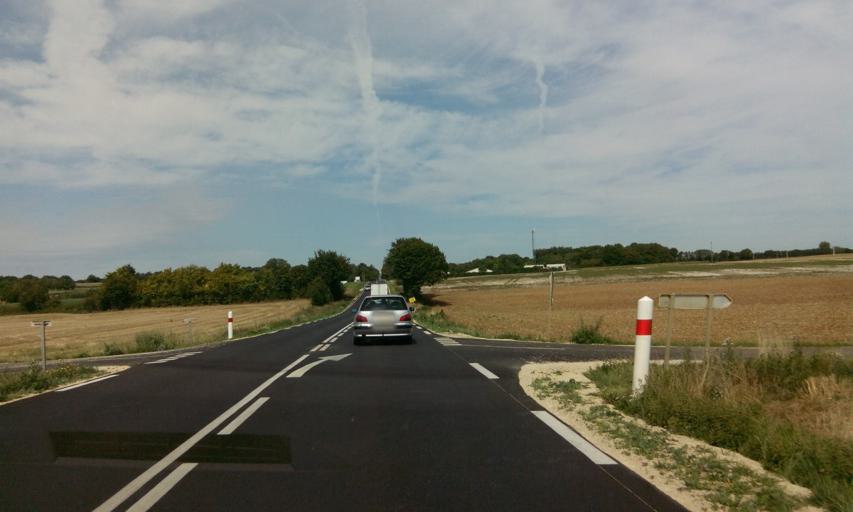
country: FR
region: Poitou-Charentes
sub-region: Departement des Deux-Sevres
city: Sauze-Vaussais
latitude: 46.1464
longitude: 0.0751
